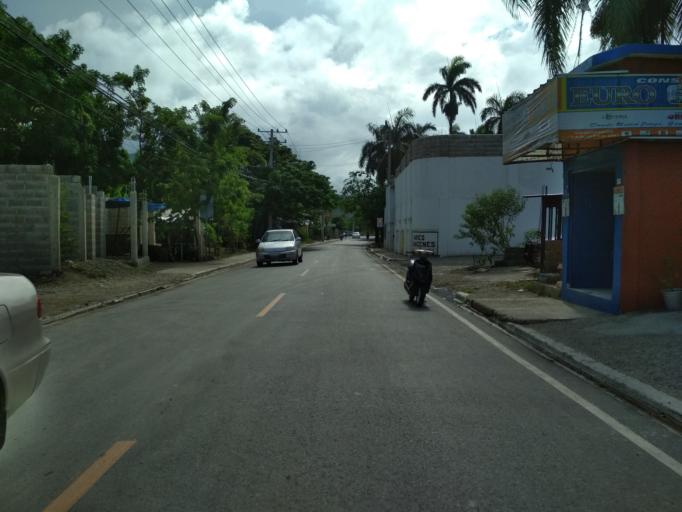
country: DO
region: Puerto Plata
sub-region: Puerto Plata
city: Puerto Plata
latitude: 19.8054
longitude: -70.7154
